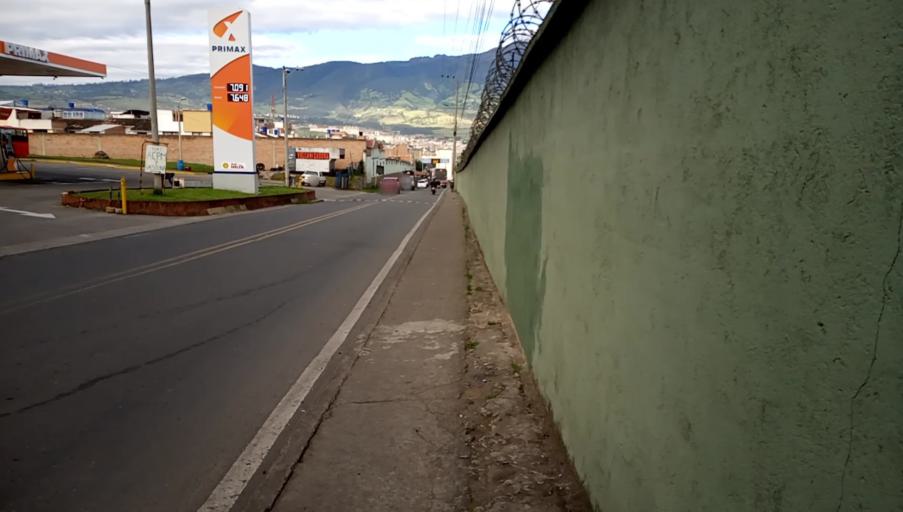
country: CO
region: Narino
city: Puerres
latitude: 1.2057
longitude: -77.2555
